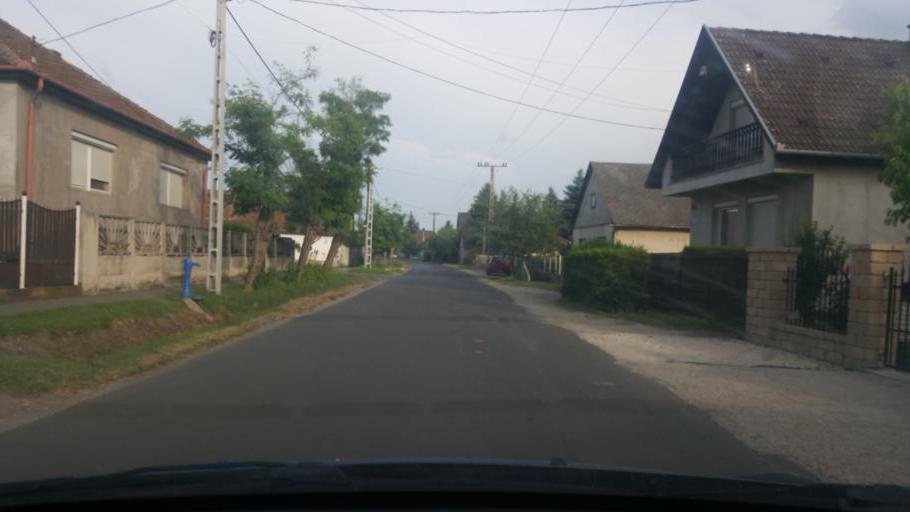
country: HU
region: Pest
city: Monor
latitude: 47.3403
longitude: 19.4436
